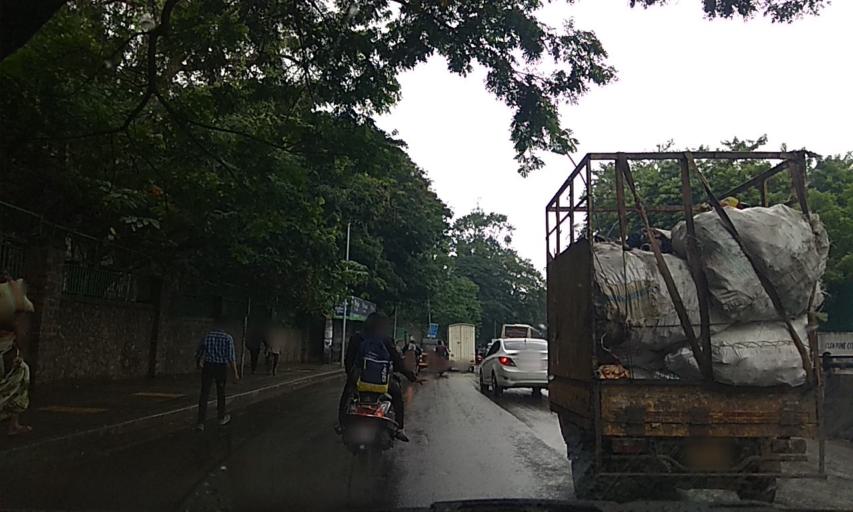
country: IN
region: Maharashtra
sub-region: Pune Division
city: Shivaji Nagar
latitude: 18.5286
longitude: 73.8501
